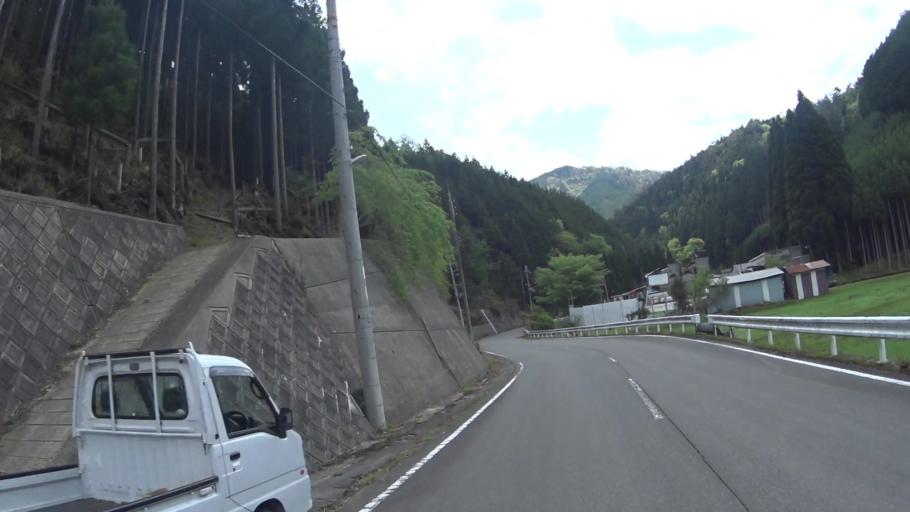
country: JP
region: Kyoto
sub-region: Kyoto-shi
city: Kamigyo-ku
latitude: 35.1176
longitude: 135.7047
